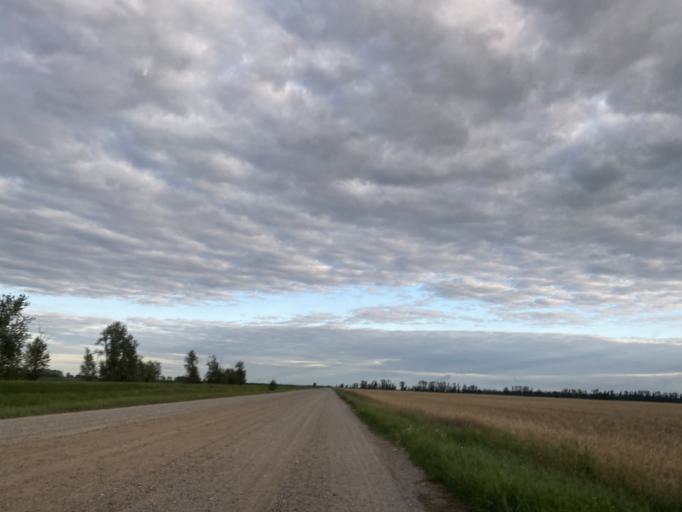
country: BY
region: Brest
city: Tsyelyakhany
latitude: 52.4907
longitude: 25.5722
